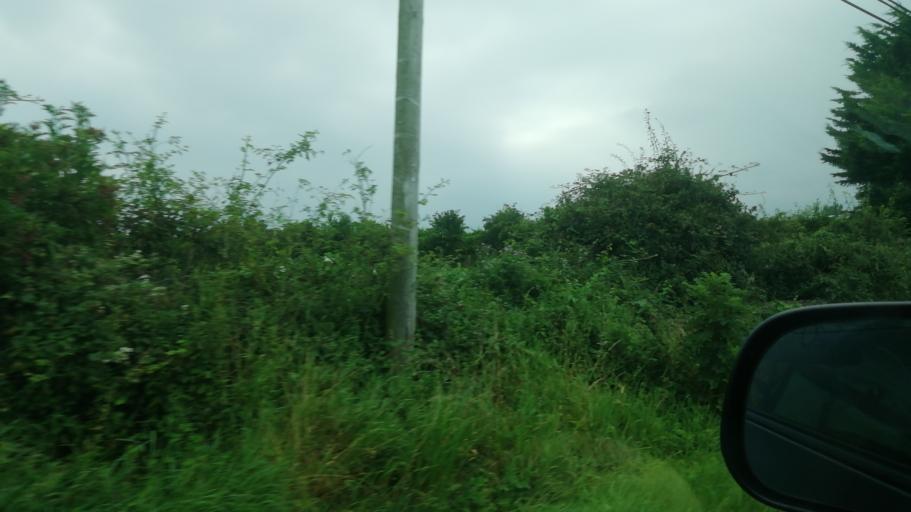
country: IE
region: Munster
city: Fethard
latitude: 52.4751
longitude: -7.6921
